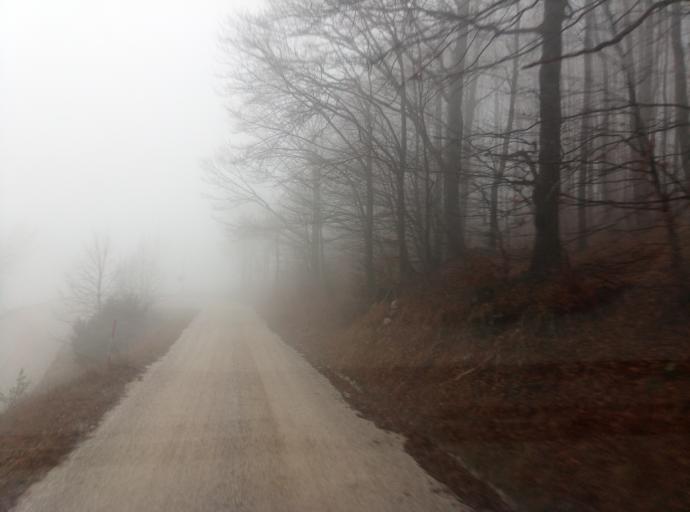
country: SI
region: Vipava
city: Vipava
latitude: 45.8987
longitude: 14.0363
